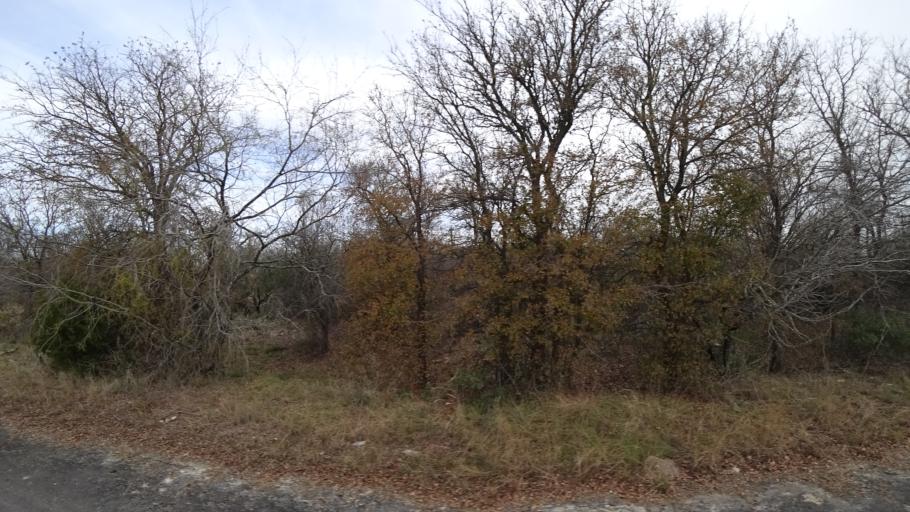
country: US
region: Texas
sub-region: Travis County
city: Garfield
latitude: 30.1119
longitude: -97.5696
